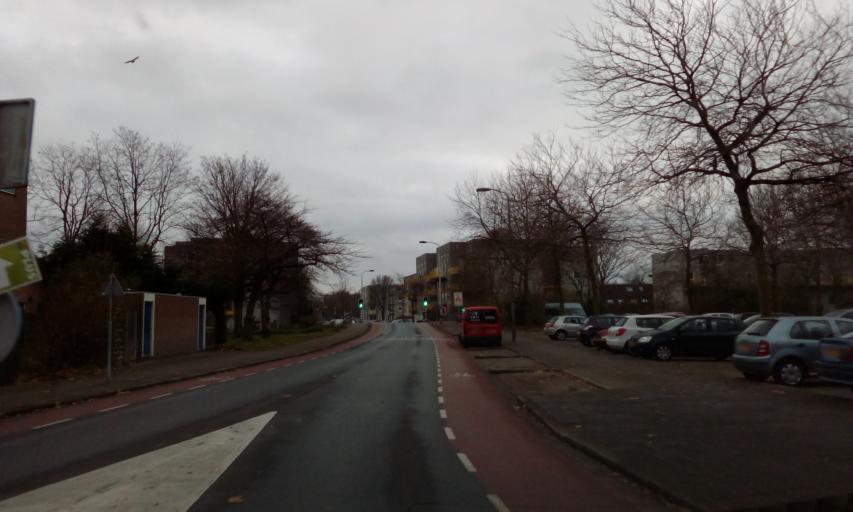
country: NL
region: South Holland
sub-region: Gemeente Delft
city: Delft
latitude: 51.9821
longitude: 4.3469
